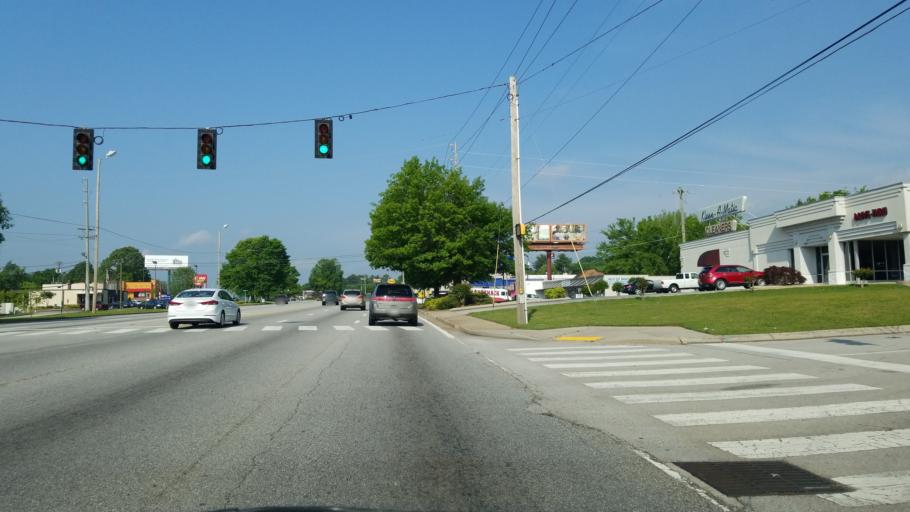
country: US
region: Tennessee
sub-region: Hamilton County
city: East Chattanooga
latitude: 35.0848
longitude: -85.1986
